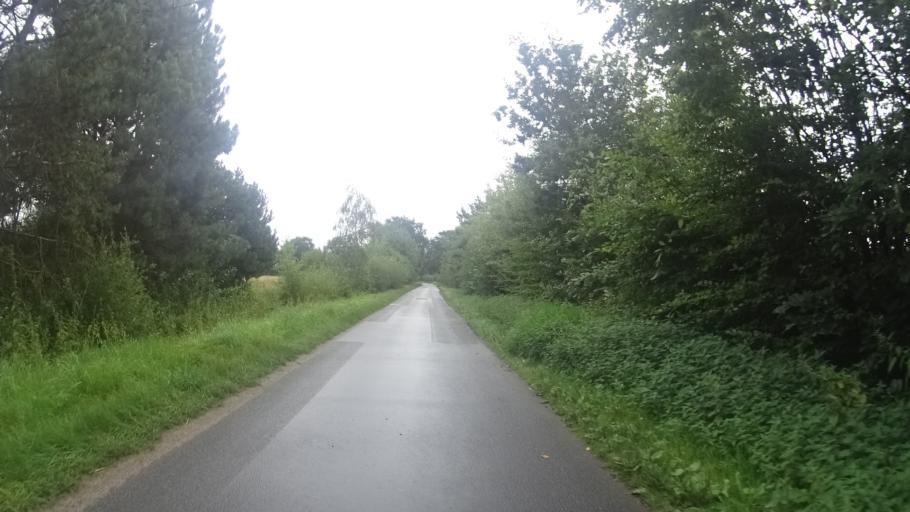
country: DE
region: Schleswig-Holstein
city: Bevern
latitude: 53.7586
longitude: 9.7856
